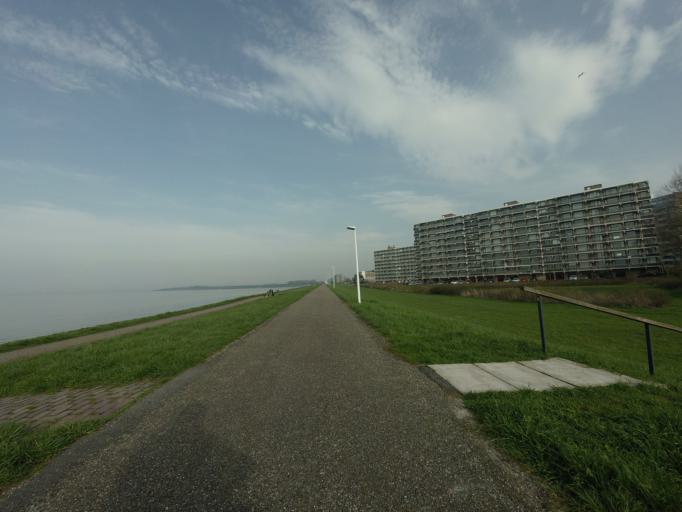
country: NL
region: Zeeland
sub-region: Gemeente Terneuzen
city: Terneuzen
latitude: 51.3352
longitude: 3.8492
